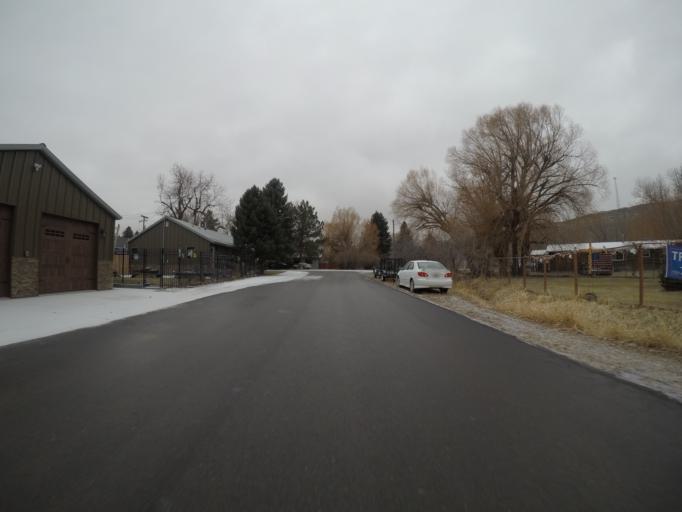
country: US
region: Montana
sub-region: Stillwater County
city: Absarokee
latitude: 45.5199
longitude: -109.4444
